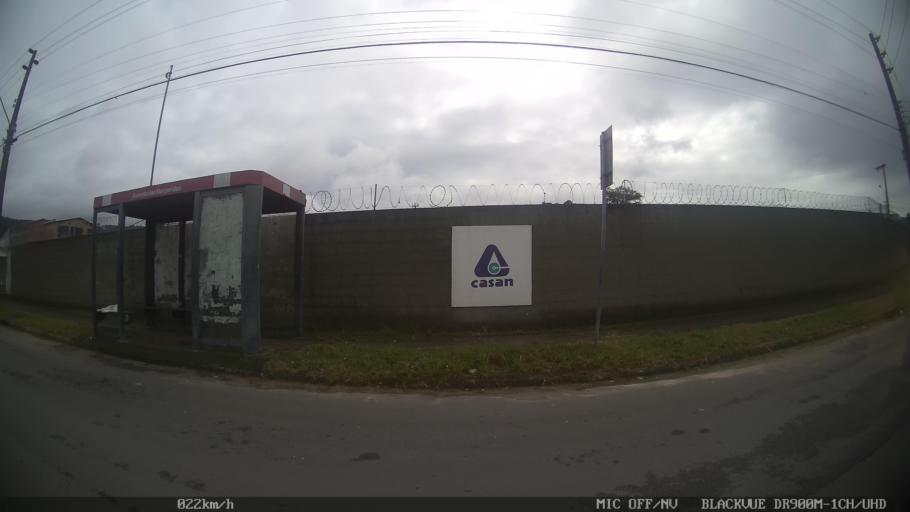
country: BR
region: Santa Catarina
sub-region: Biguacu
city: Biguacu
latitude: -27.5385
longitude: -48.6399
